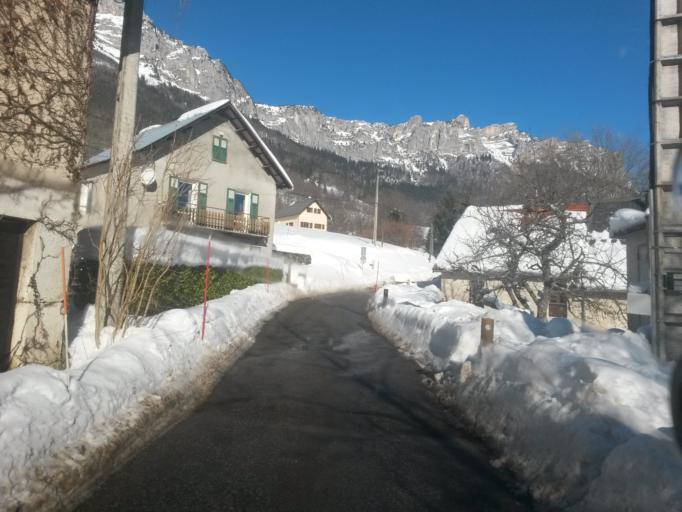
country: FR
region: Rhone-Alpes
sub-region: Departement de l'Isere
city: Lumbin
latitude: 45.3307
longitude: 5.9029
